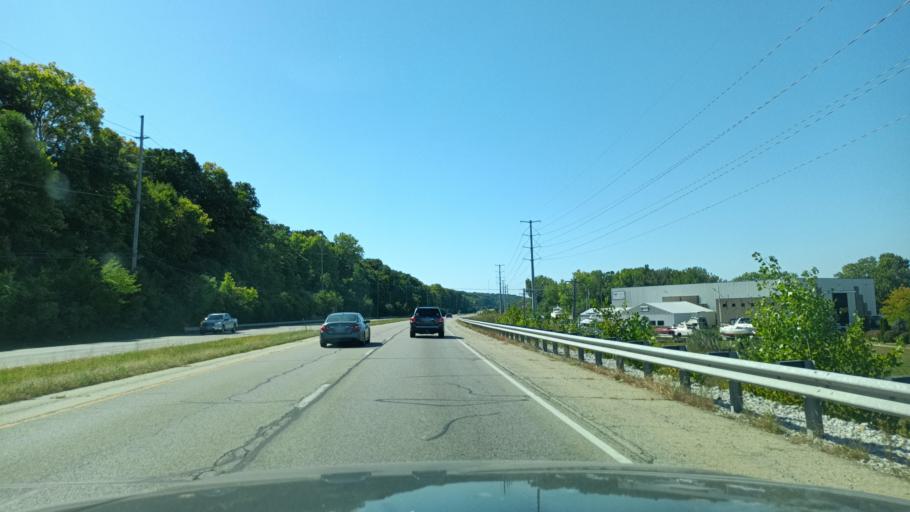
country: US
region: Illinois
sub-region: Tazewell County
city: East Peoria
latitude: 40.6925
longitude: -89.5430
